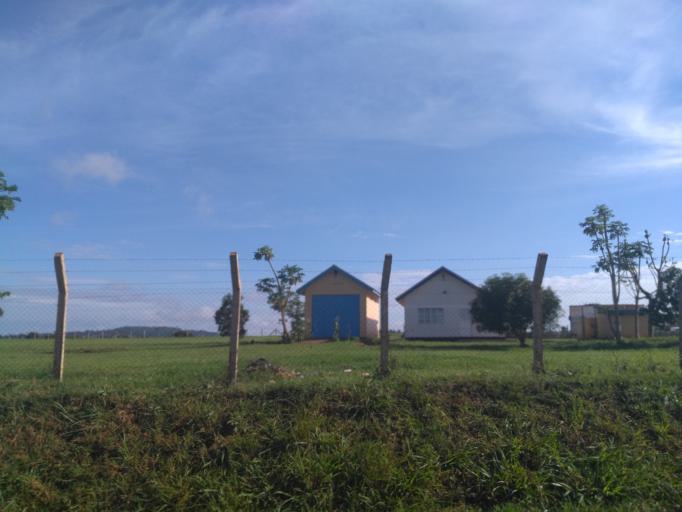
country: UG
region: Eastern Region
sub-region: Jinja District
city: Jinja
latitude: 0.4500
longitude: 33.1940
